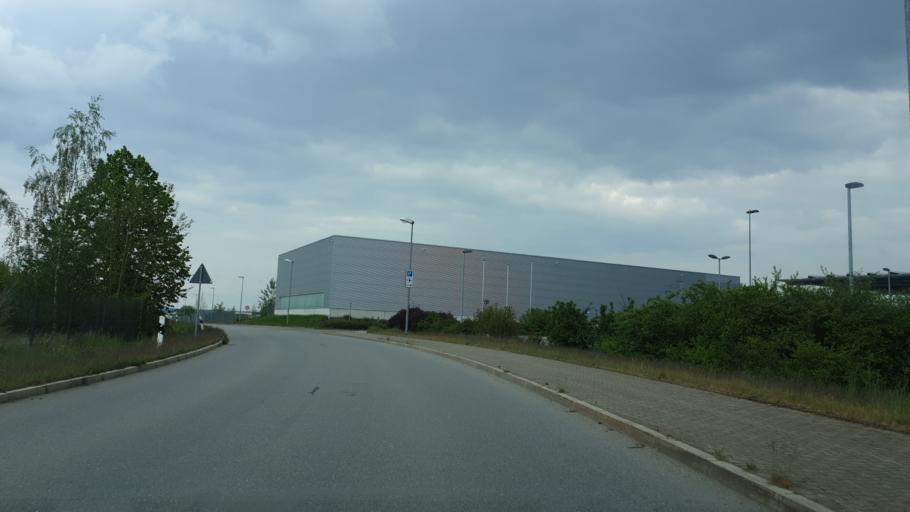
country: DE
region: Saxony
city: Jahnsdorf
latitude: 50.7482
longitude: 12.8308
